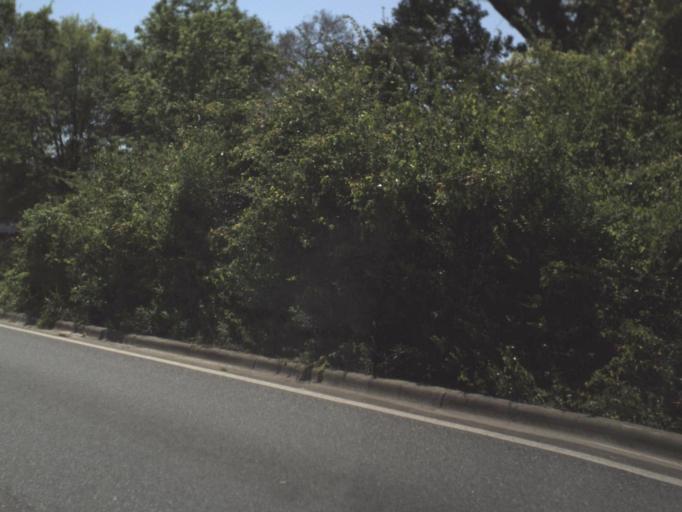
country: US
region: Florida
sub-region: Escambia County
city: Bellview
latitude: 30.4875
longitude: -87.3065
